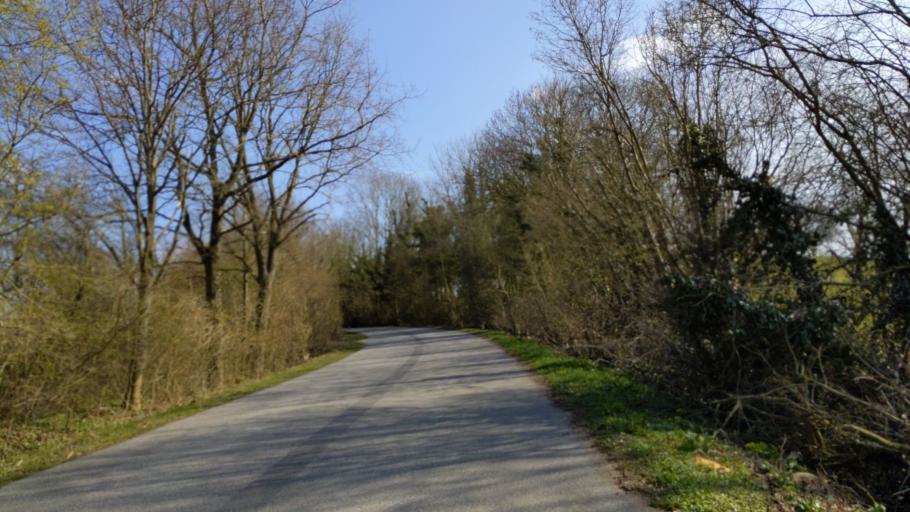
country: DE
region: Schleswig-Holstein
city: Schashagen
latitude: 54.1232
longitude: 10.8698
